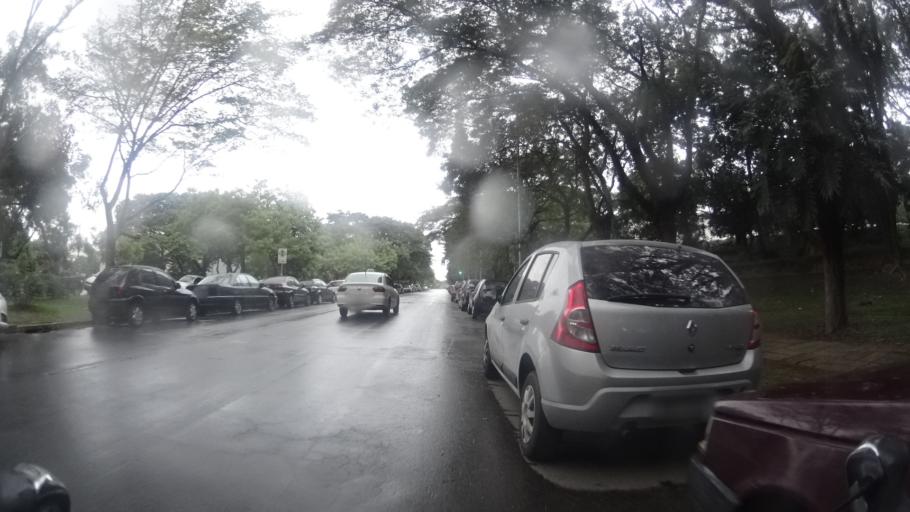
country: BR
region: Sao Paulo
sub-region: Osasco
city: Osasco
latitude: -23.5621
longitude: -46.7242
